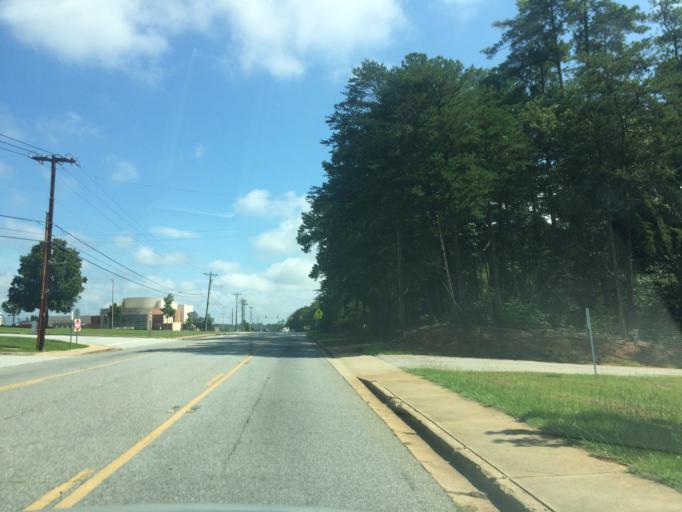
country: US
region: South Carolina
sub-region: Spartanburg County
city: Lyman
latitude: 34.9290
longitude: -82.1275
